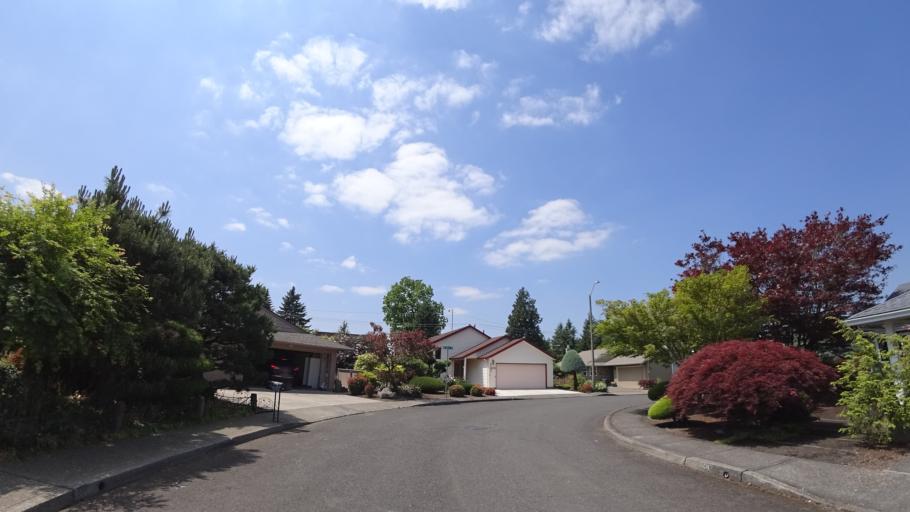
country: US
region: Oregon
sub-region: Multnomah County
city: Fairview
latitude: 45.5391
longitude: -122.5094
